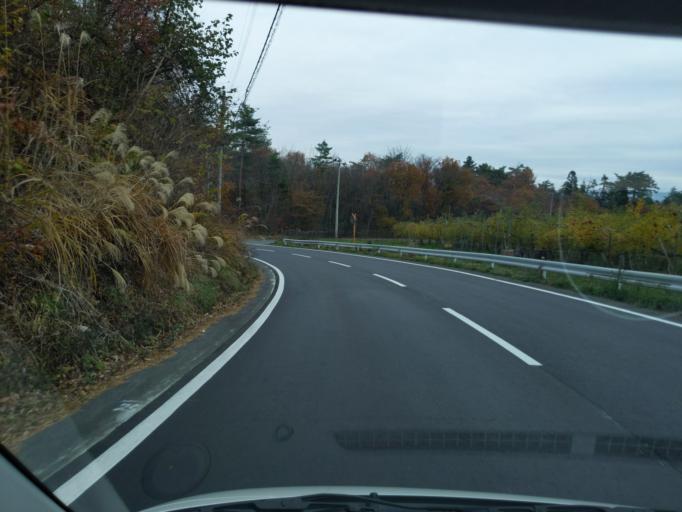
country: JP
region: Iwate
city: Kitakami
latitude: 39.2427
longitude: 141.2189
